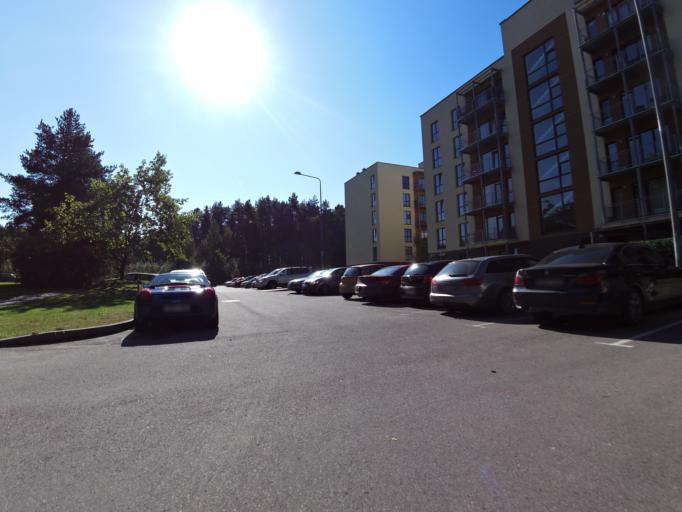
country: LT
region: Vilnius County
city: Lazdynai
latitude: 54.6801
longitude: 25.1914
